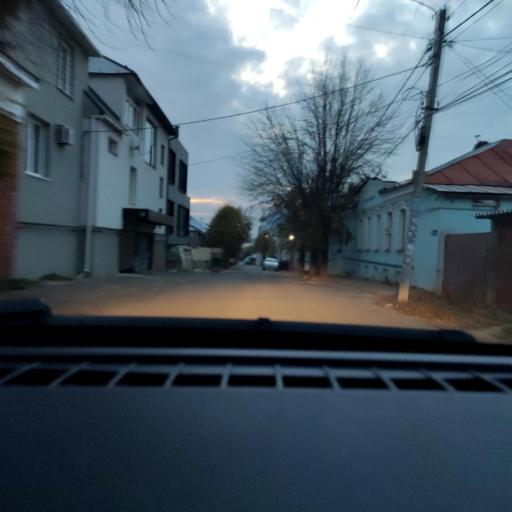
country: RU
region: Voronezj
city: Voronezh
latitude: 51.6753
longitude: 39.2201
